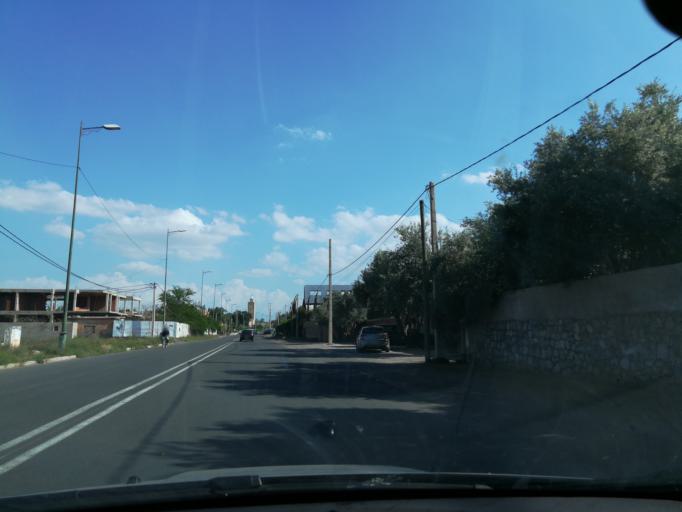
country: MA
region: Marrakech-Tensift-Al Haouz
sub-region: Marrakech
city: Marrakesh
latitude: 31.6632
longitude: -8.0557
